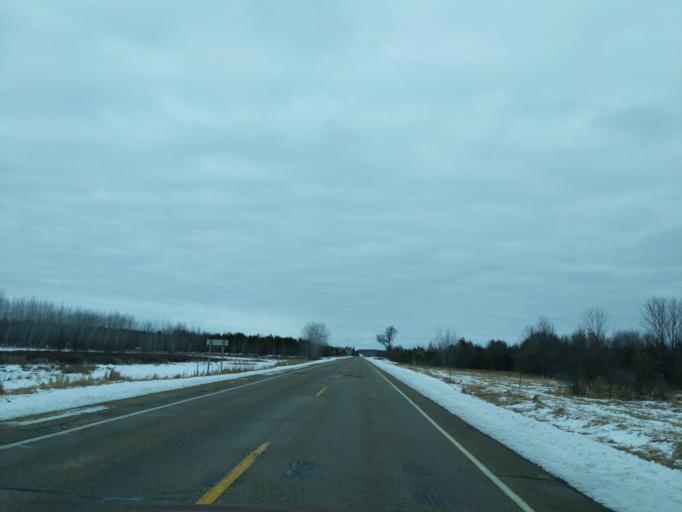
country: US
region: Wisconsin
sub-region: Waushara County
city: Wautoma
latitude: 43.9835
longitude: -89.3277
